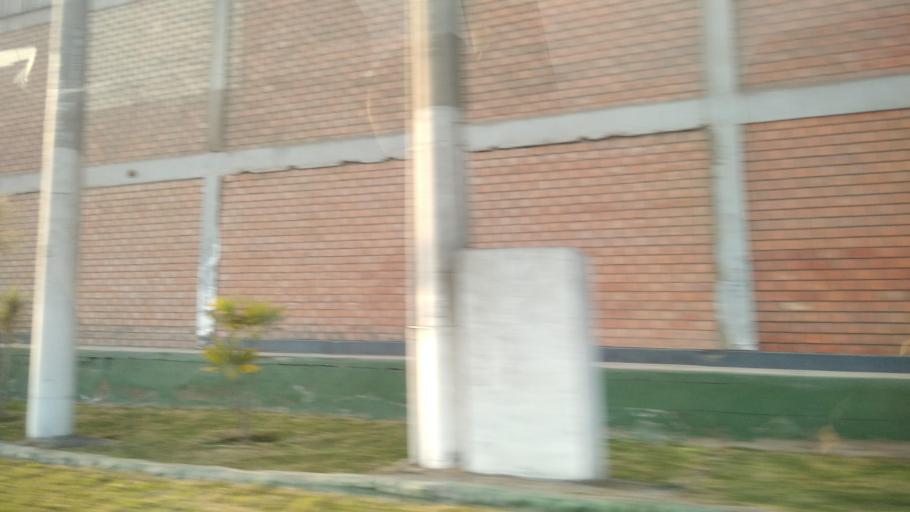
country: PE
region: Lima
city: Lima
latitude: -12.0183
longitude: -76.9885
